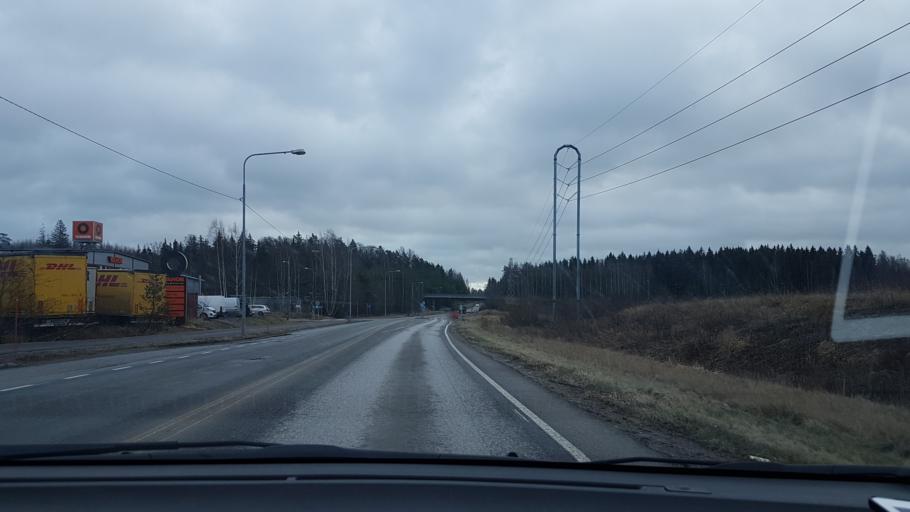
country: FI
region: Uusimaa
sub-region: Helsinki
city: Tuusula
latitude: 60.3792
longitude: 25.0498
